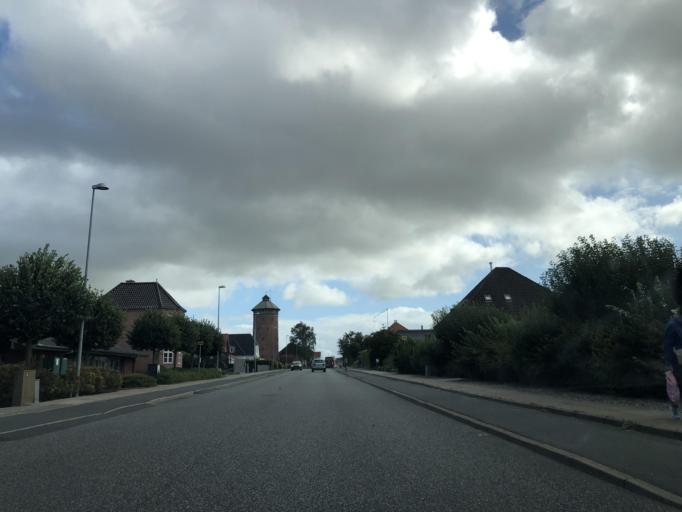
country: DK
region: Central Jutland
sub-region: Randers Kommune
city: Randers
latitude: 56.4707
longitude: 10.0159
